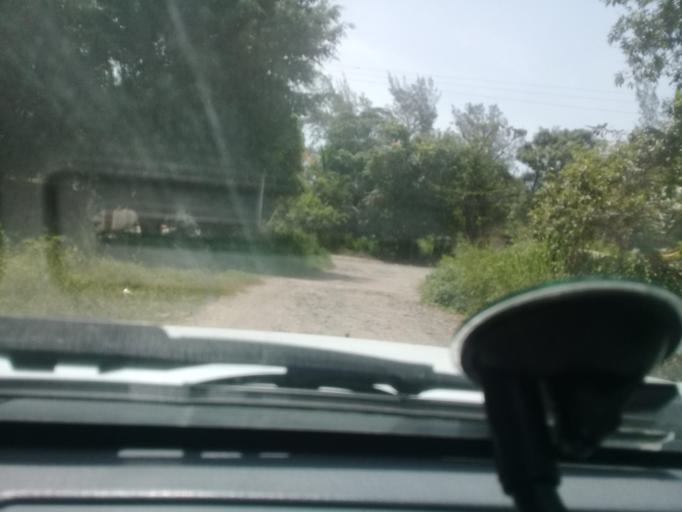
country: MX
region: Veracruz
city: Anahuac
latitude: 22.2289
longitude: -97.8323
